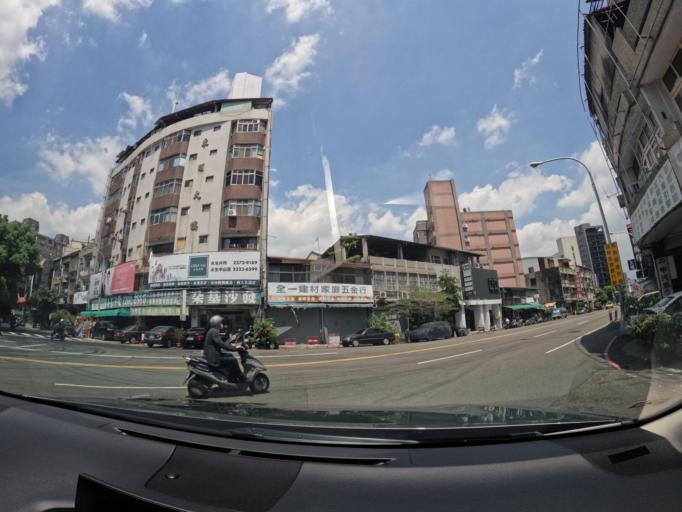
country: TW
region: Taiwan
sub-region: Taichung City
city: Taichung
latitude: 24.1561
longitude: 120.6683
